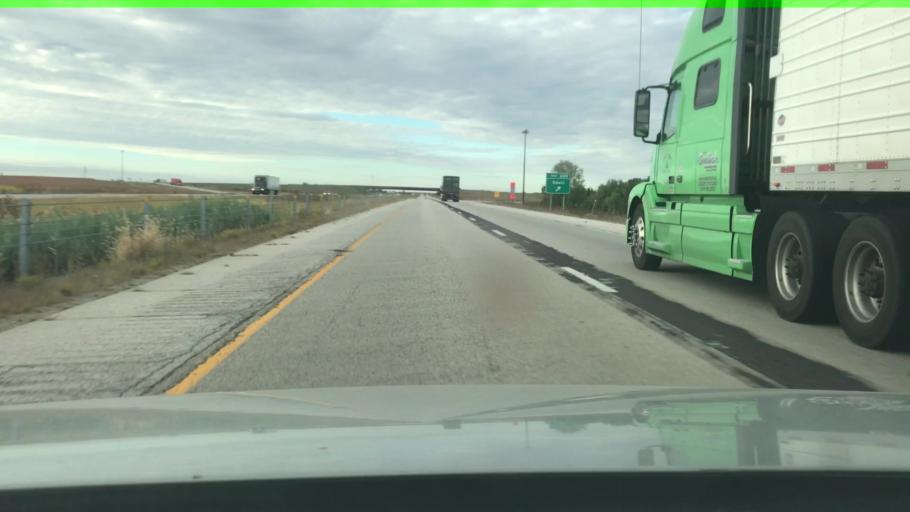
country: US
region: Illinois
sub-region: Livingston County
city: Odell
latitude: 41.0120
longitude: -88.5350
